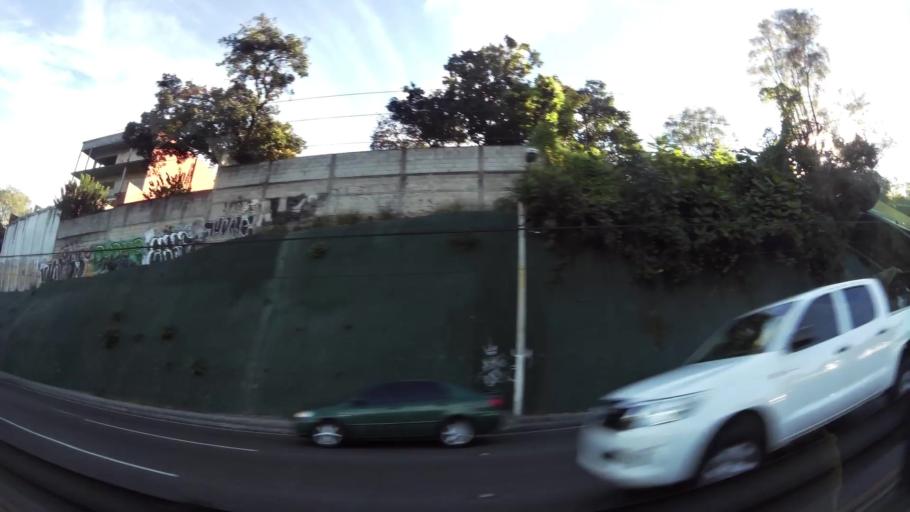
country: GT
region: Guatemala
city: Guatemala City
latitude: 14.6071
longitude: -90.5020
